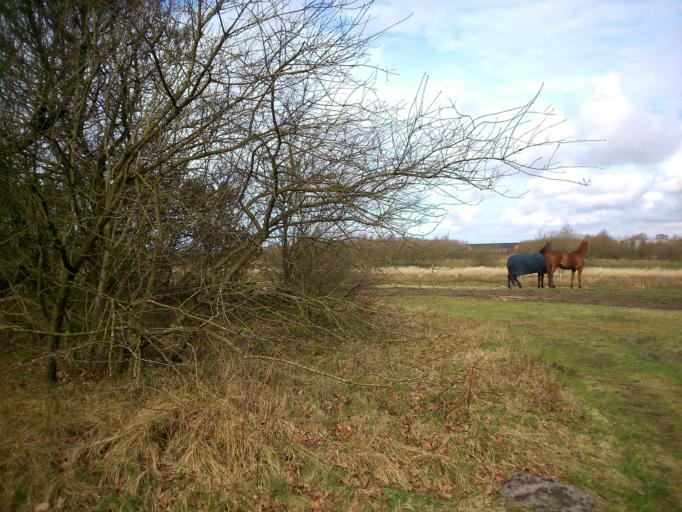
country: DK
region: Central Jutland
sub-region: Ringkobing-Skjern Kommune
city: Skjern
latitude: 55.9512
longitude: 8.5224
